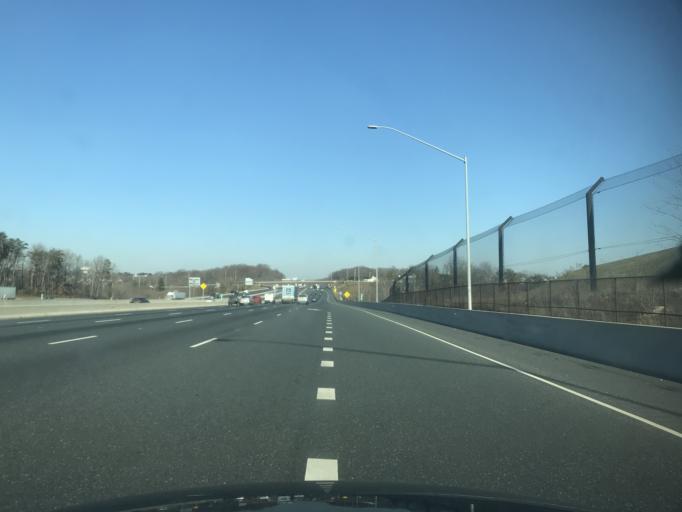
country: US
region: Maryland
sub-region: Baltimore County
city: White Marsh
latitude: 39.3833
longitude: -76.4434
